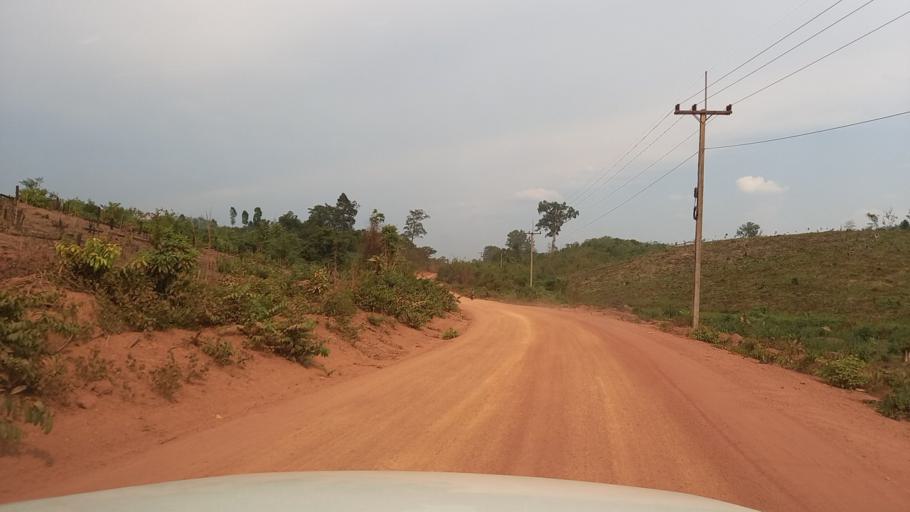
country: LA
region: Bolikhamxai
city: Bolikhan
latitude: 18.5410
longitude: 103.7986
